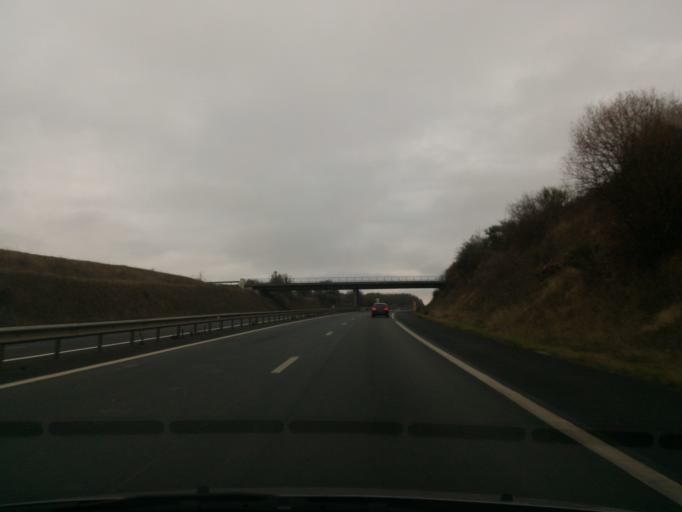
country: FR
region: Poitou-Charentes
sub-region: Departement de la Vienne
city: Fontaine-le-Comte
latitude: 46.5188
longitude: 0.2790
